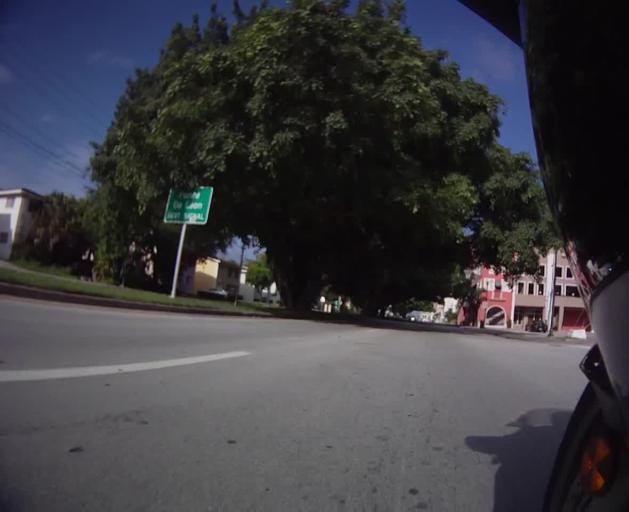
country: US
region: Florida
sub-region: Miami-Dade County
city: Coral Gables
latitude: 25.7348
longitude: -80.2615
